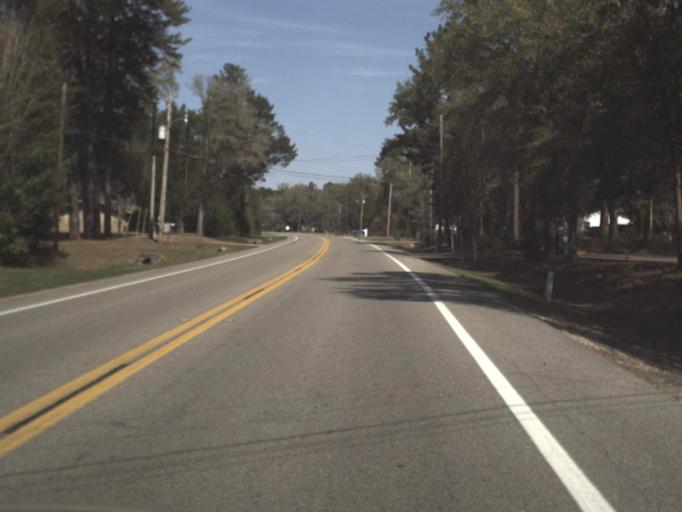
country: US
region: Florida
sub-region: Liberty County
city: Bristol
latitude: 30.4377
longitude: -84.9739
